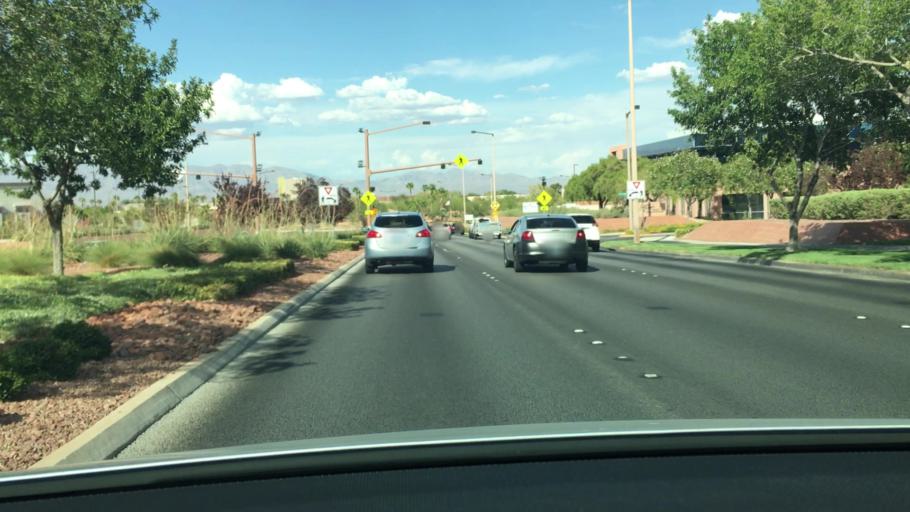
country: US
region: Nevada
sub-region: Clark County
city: Summerlin South
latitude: 36.1879
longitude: -115.3055
